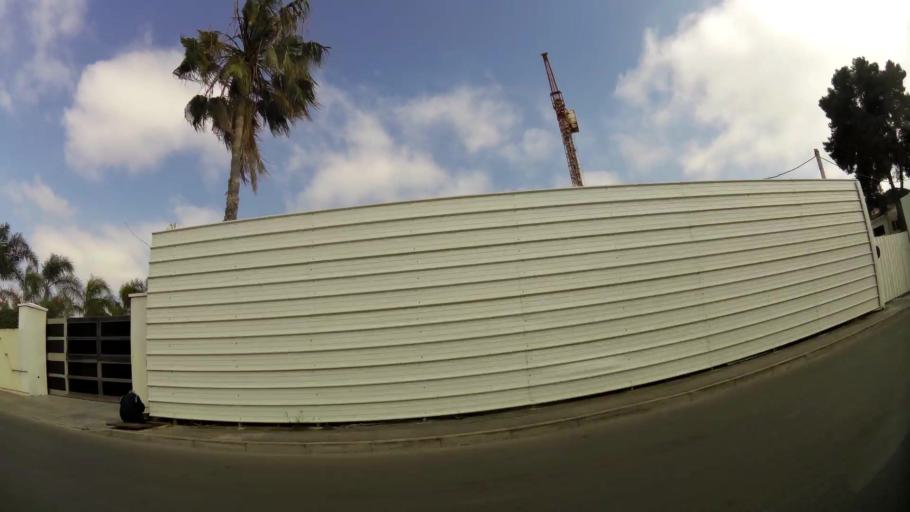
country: MA
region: Rabat-Sale-Zemmour-Zaer
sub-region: Rabat
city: Rabat
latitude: 33.9783
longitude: -6.8492
